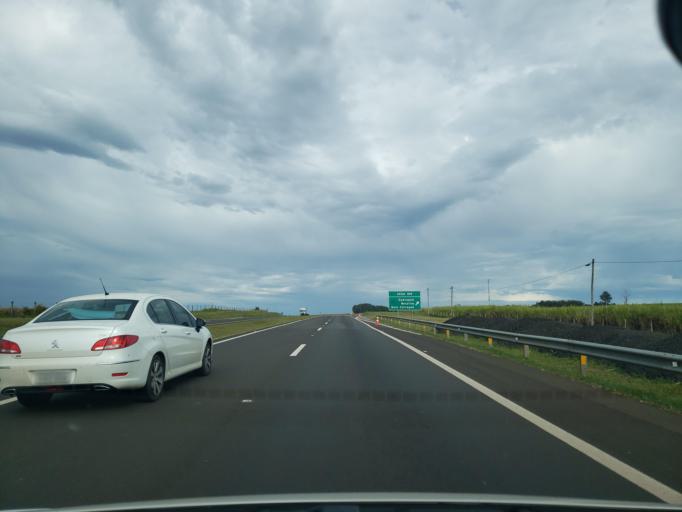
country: BR
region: Sao Paulo
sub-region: Dois Corregos
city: Dois Corregos
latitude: -22.2629
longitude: -48.3772
